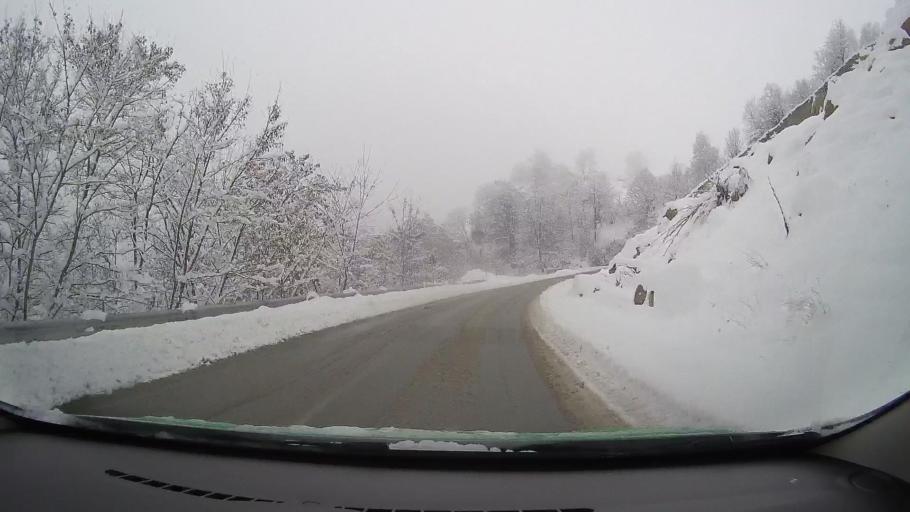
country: RO
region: Sibiu
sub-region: Comuna Jina
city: Jina
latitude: 45.7712
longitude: 23.6671
